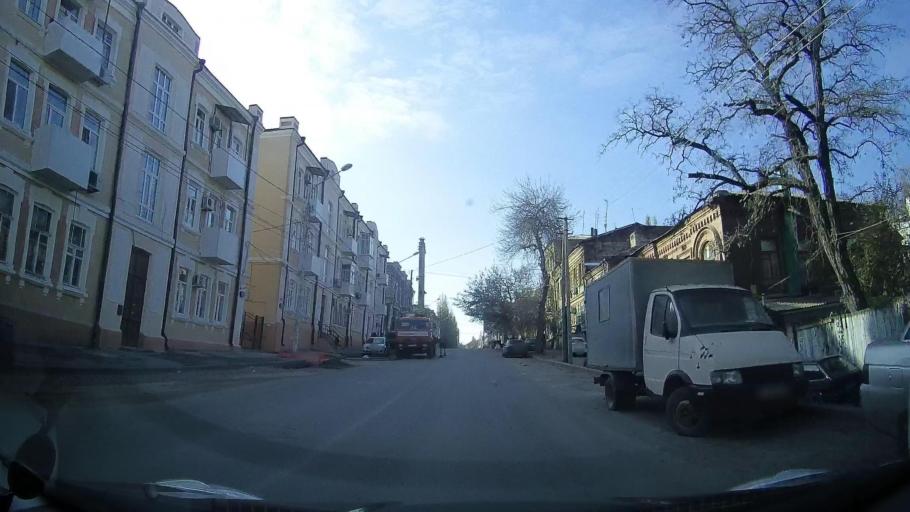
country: RU
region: Rostov
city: Rostov-na-Donu
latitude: 47.2198
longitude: 39.7319
